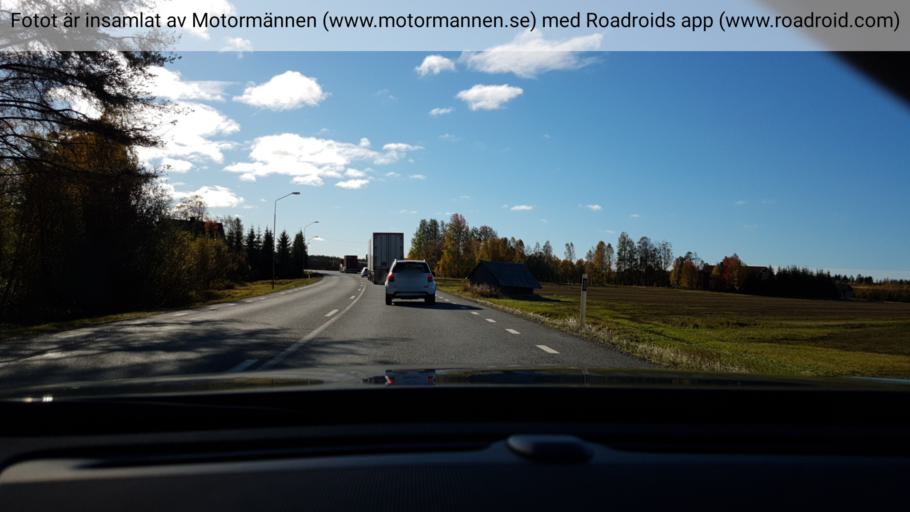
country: SE
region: Vaesterbotten
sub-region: Skelleftea Kommun
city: Burea
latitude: 64.5111
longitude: 21.2568
